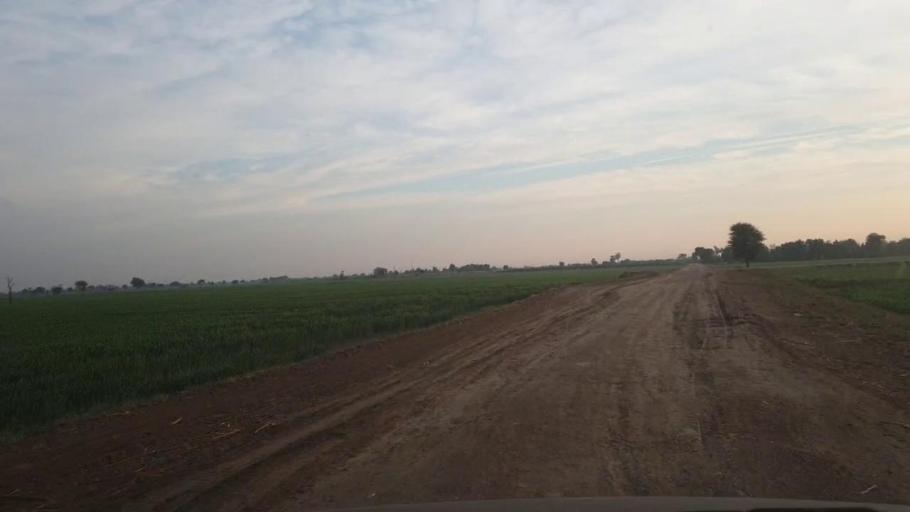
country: PK
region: Sindh
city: Shahpur Chakar
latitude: 26.0555
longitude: 68.5323
